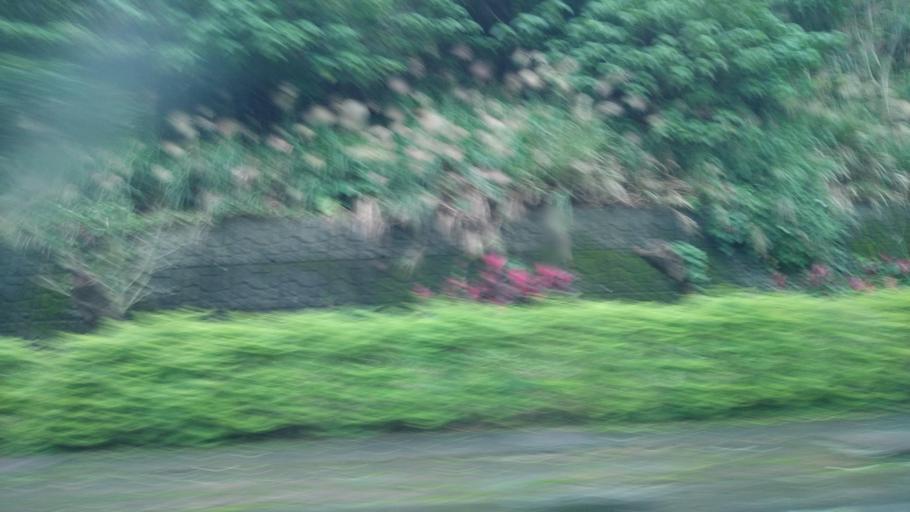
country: TW
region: Taiwan
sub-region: Yilan
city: Yilan
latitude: 24.5980
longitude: 121.8351
